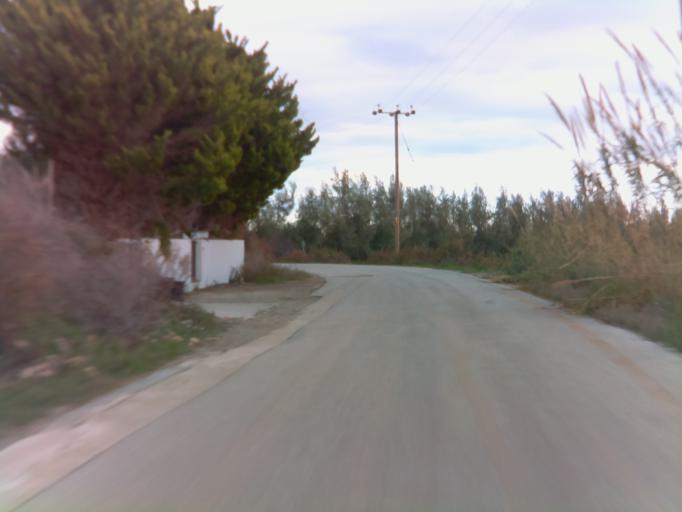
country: CY
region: Pafos
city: Pegeia
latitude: 34.8793
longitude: 32.3353
